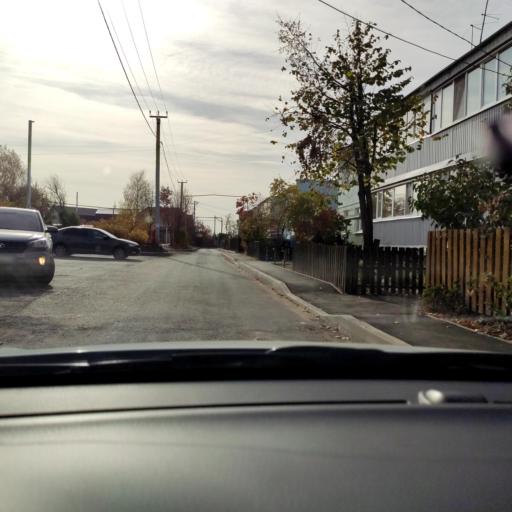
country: RU
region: Tatarstan
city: Vysokaya Gora
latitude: 55.8077
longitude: 49.2719
